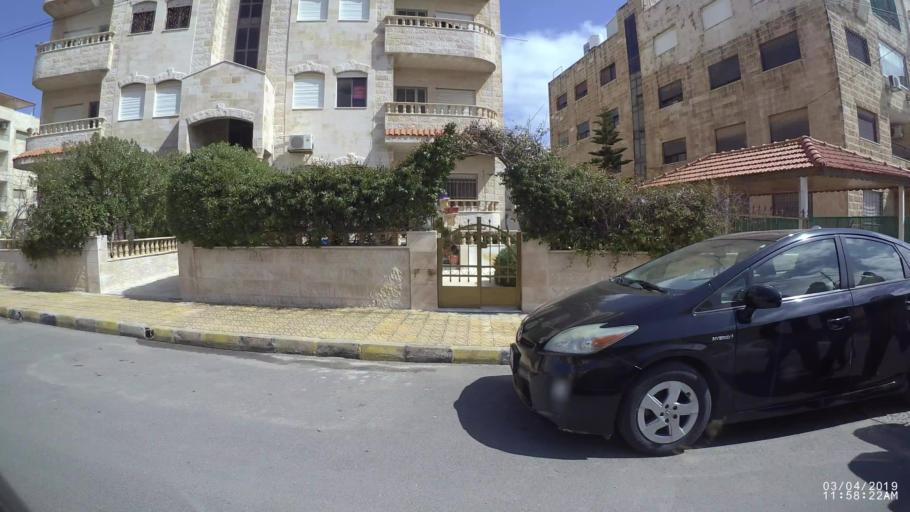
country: JO
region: Amman
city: Wadi as Sir
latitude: 31.9595
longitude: 35.8427
